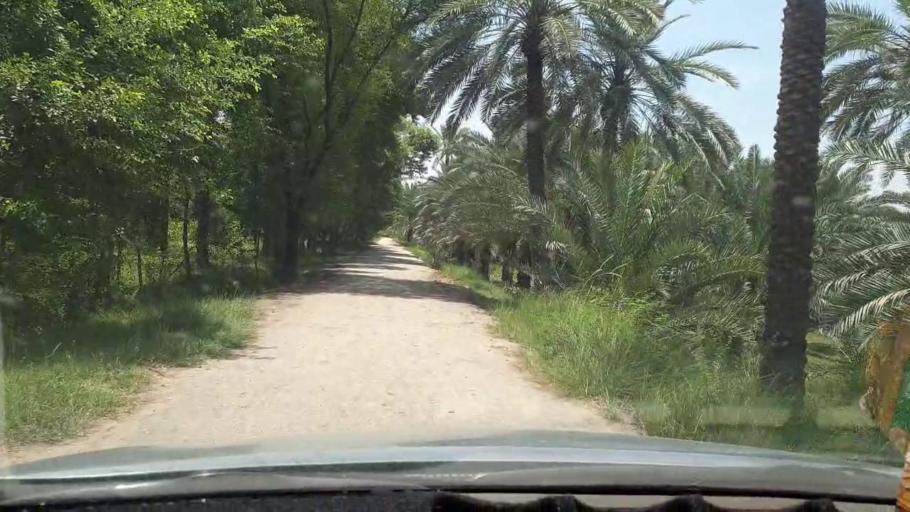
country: PK
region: Sindh
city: Khairpur
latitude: 27.4540
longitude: 68.7813
